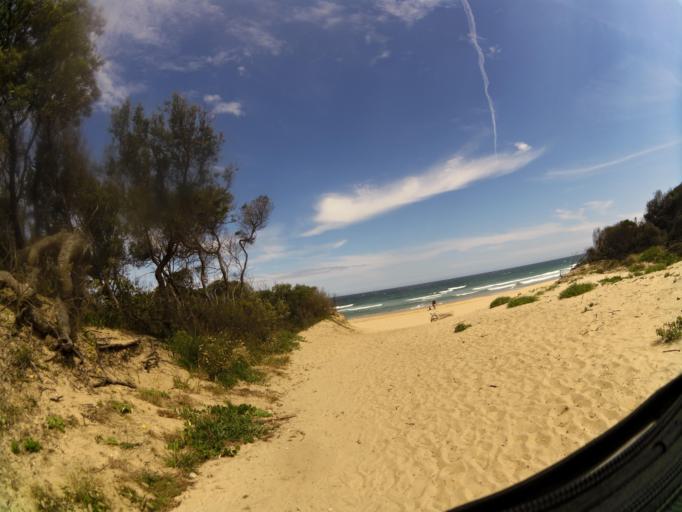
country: AU
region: Victoria
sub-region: East Gippsland
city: Lakes Entrance
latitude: -37.8053
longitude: 148.6346
